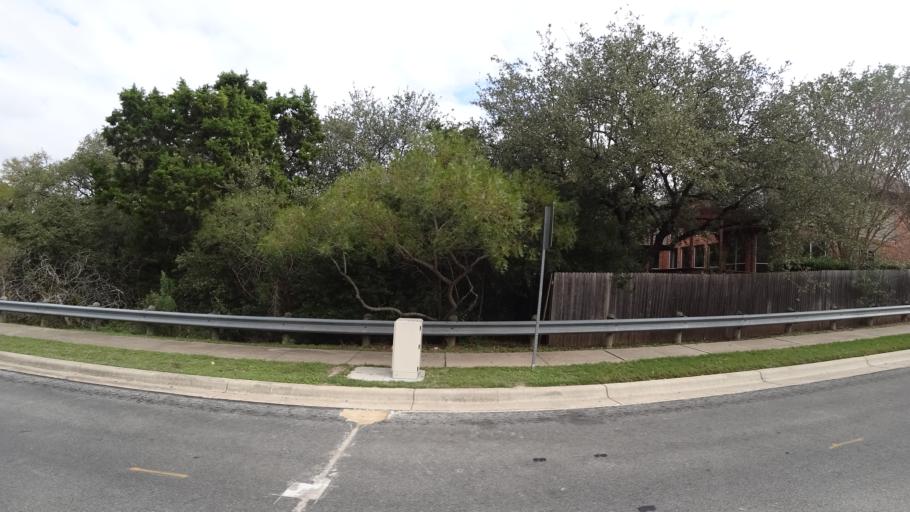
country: US
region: Texas
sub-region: Travis County
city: Shady Hollow
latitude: 30.2185
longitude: -97.8881
